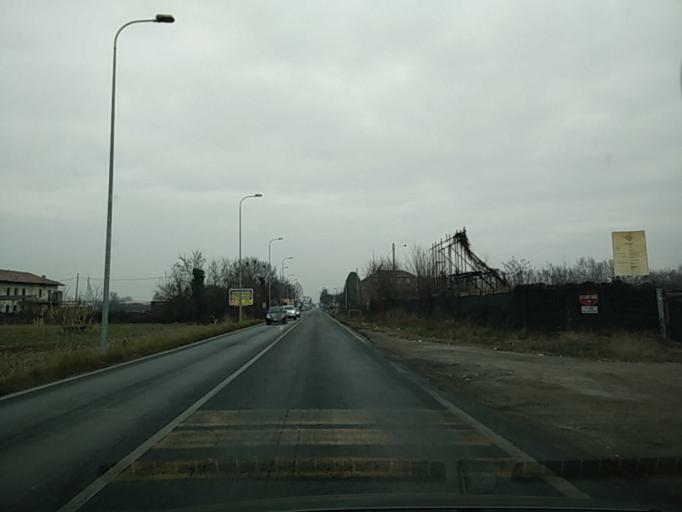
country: IT
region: Piedmont
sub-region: Provincia di Torino
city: Leini
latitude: 45.1537
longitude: 7.7089
